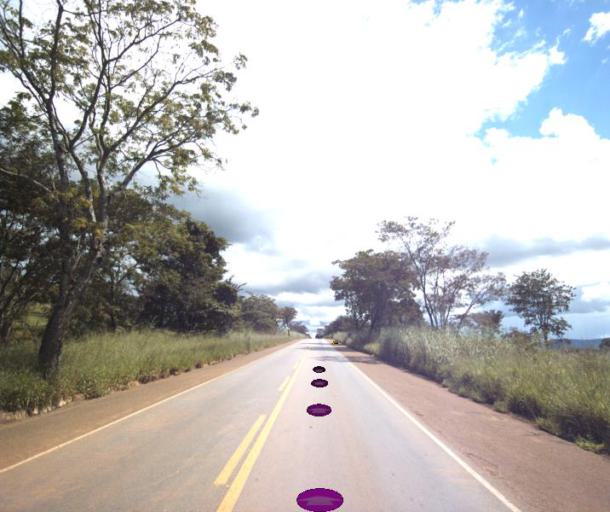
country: BR
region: Goias
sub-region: Anapolis
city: Anapolis
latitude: -16.0913
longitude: -49.0368
